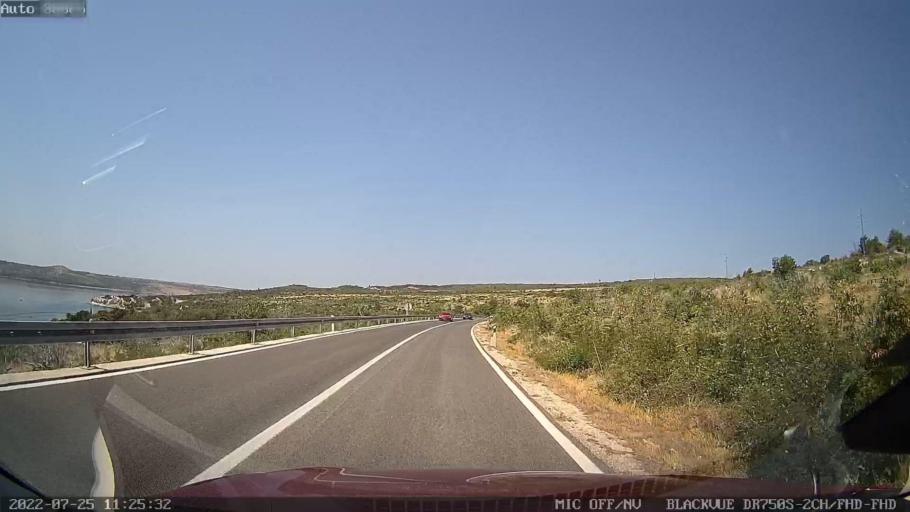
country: HR
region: Zadarska
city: Posedarje
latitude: 44.2224
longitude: 15.5203
